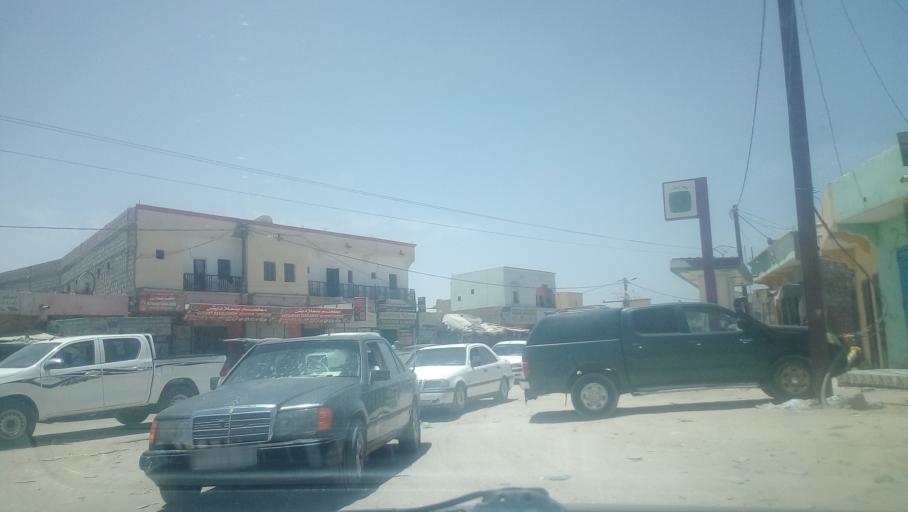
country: MR
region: Nouakchott
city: Nouakchott
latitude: 18.0558
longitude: -15.9618
